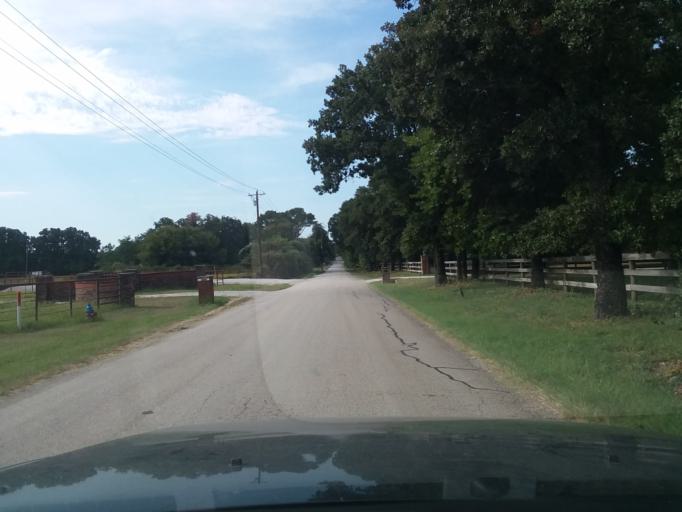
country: US
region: Texas
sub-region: Denton County
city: Copper Canyon
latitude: 33.1119
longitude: -97.1311
